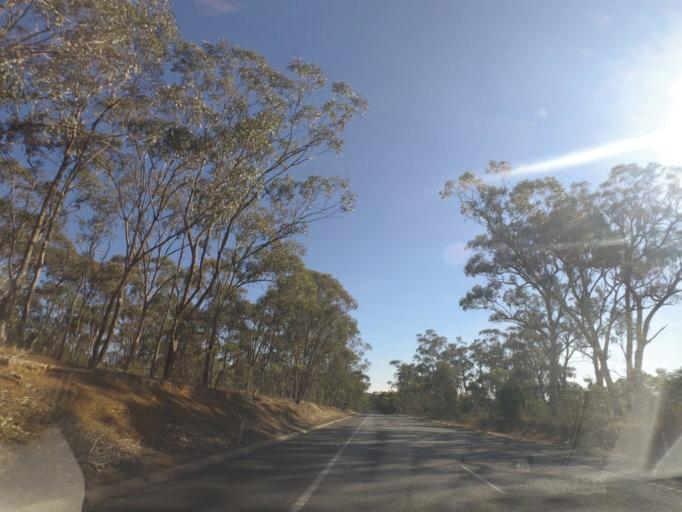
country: AU
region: Victoria
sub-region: Murrindindi
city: Kinglake West
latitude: -37.1750
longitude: 145.0731
